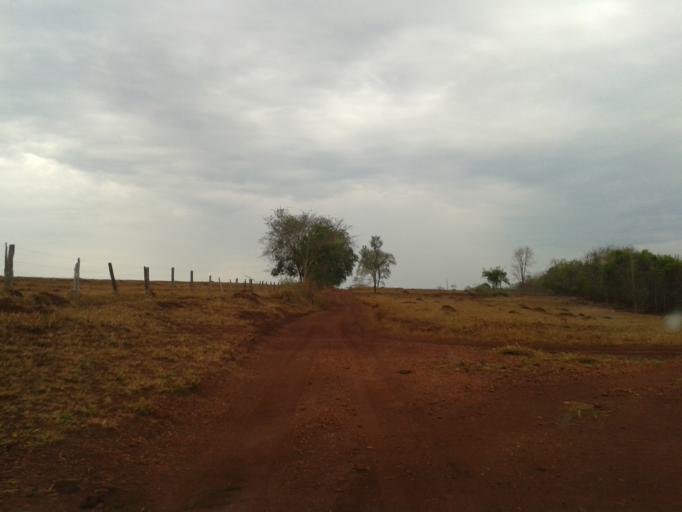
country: BR
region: Minas Gerais
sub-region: Santa Vitoria
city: Santa Vitoria
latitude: -18.8573
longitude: -49.8275
